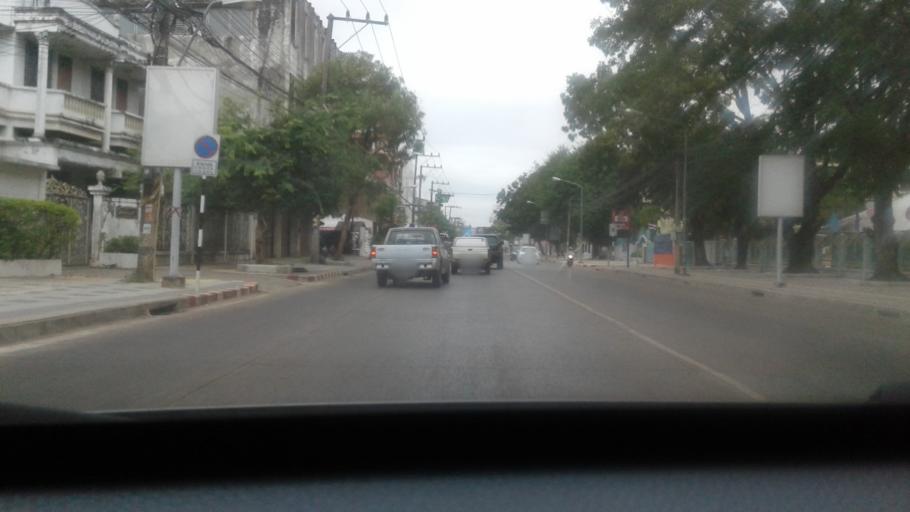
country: TH
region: Changwat Udon Thani
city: Udon Thani
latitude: 17.4025
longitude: 102.7915
